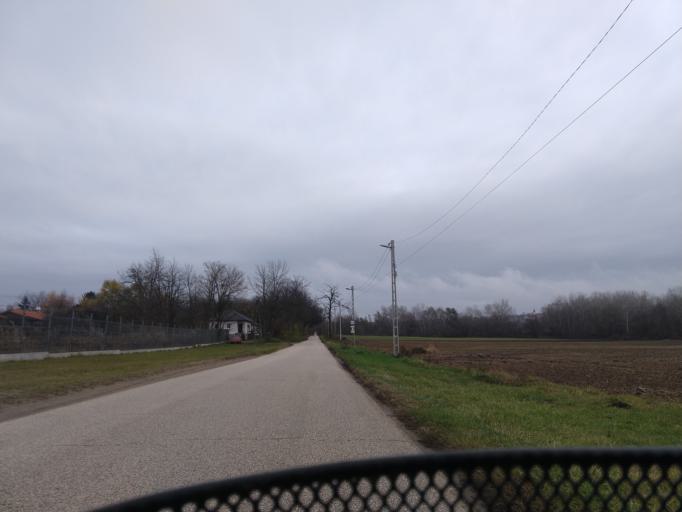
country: HU
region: Pest
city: Erdokertes
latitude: 47.6653
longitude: 19.2896
